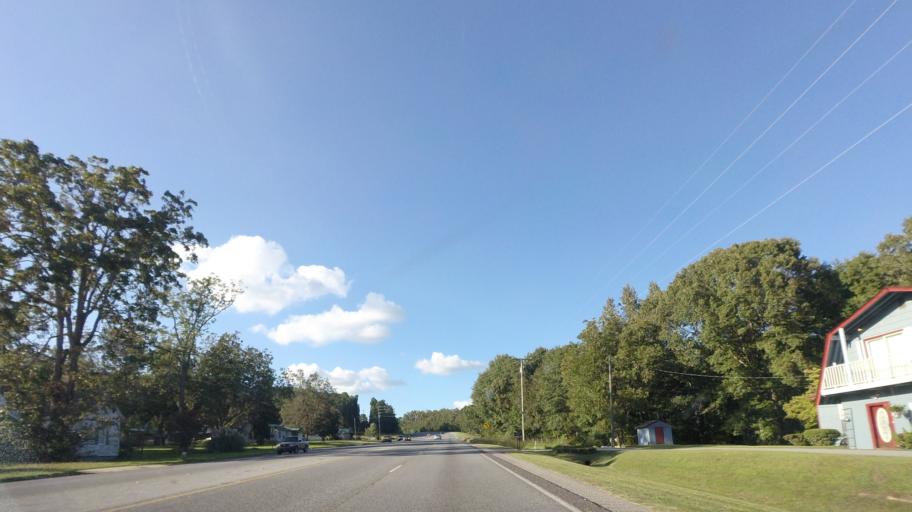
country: US
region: Georgia
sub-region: Pike County
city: Zebulon
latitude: 33.0231
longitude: -84.3245
